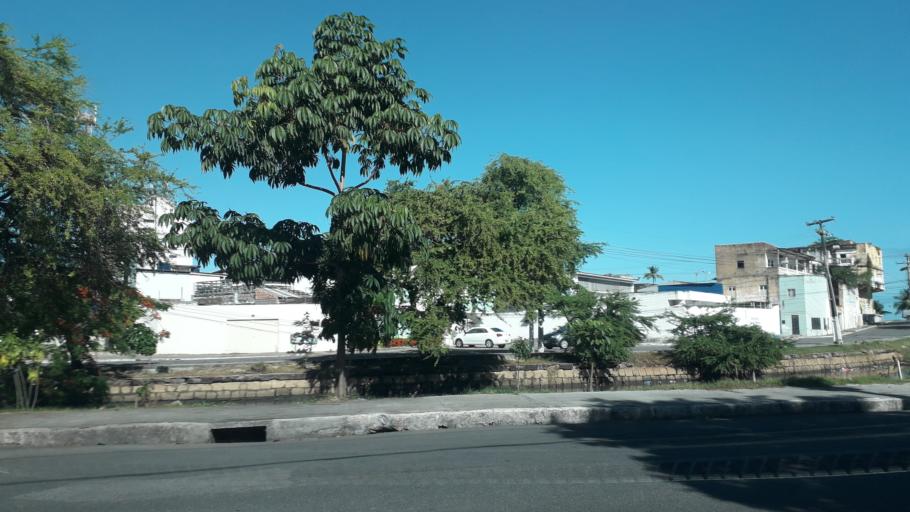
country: BR
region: Alagoas
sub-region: Maceio
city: Maceio
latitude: -9.6683
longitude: -35.7306
